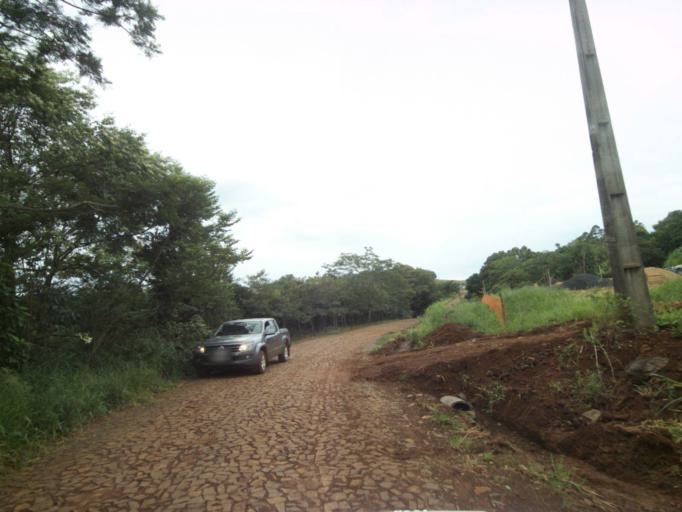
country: BR
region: Parana
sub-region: Guaraniacu
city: Guaraniacu
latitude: -25.1167
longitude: -52.8571
